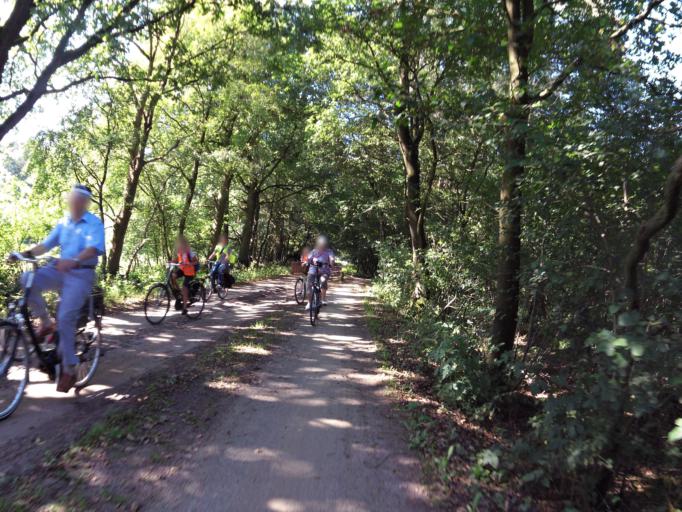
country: NL
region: Overijssel
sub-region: Gemeente Haaksbergen
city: Haaksbergen
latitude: 52.1515
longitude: 6.7983
